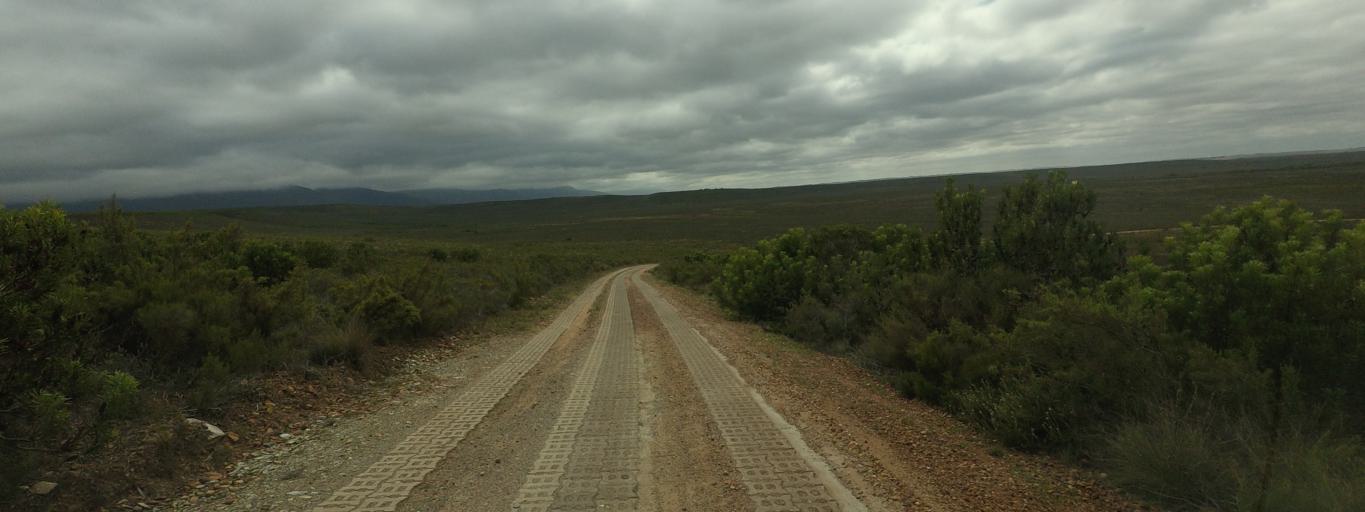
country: ZA
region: Western Cape
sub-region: Overberg District Municipality
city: Swellendam
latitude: -34.0625
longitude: 20.4362
